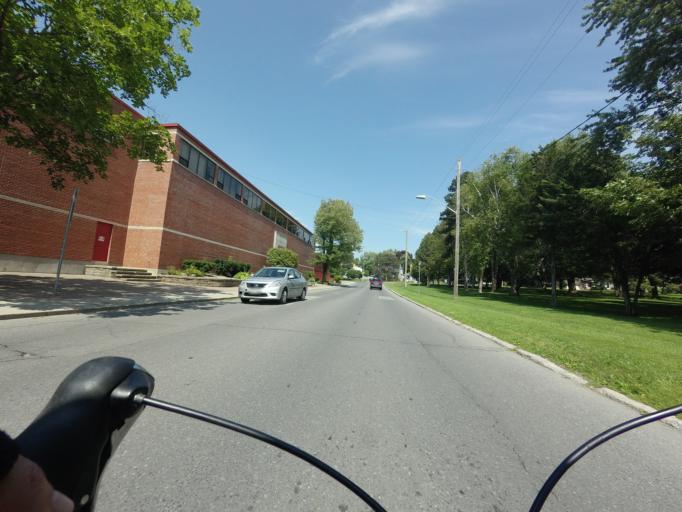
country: CA
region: Ontario
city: Brockville
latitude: 44.5986
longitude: -75.6774
